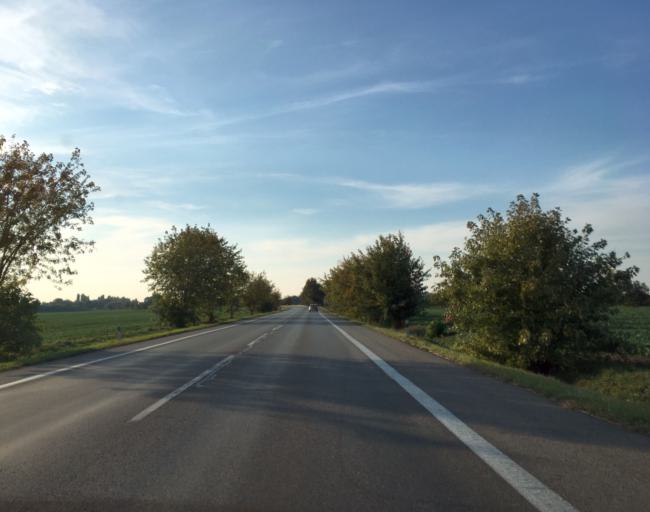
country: SK
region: Nitriansky
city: Sellye
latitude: 48.1511
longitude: 17.9515
